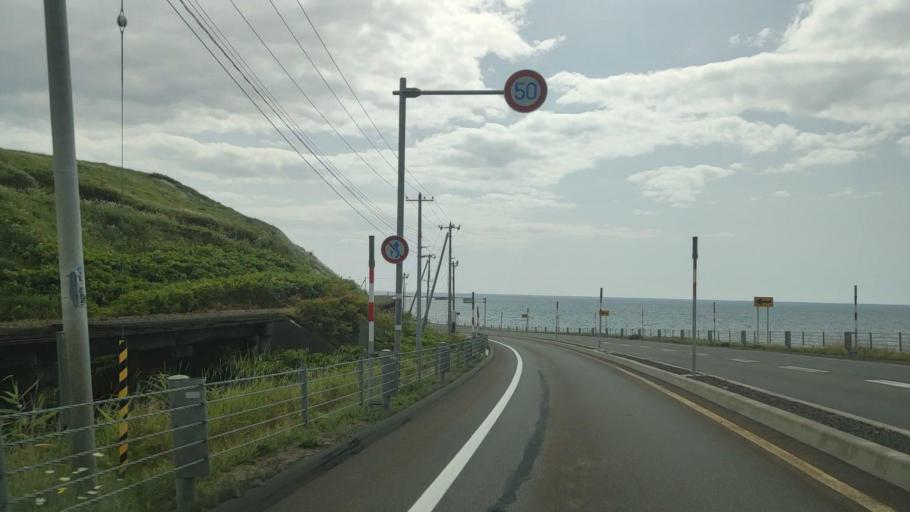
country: JP
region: Hokkaido
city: Rumoi
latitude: 44.5463
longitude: 141.7670
